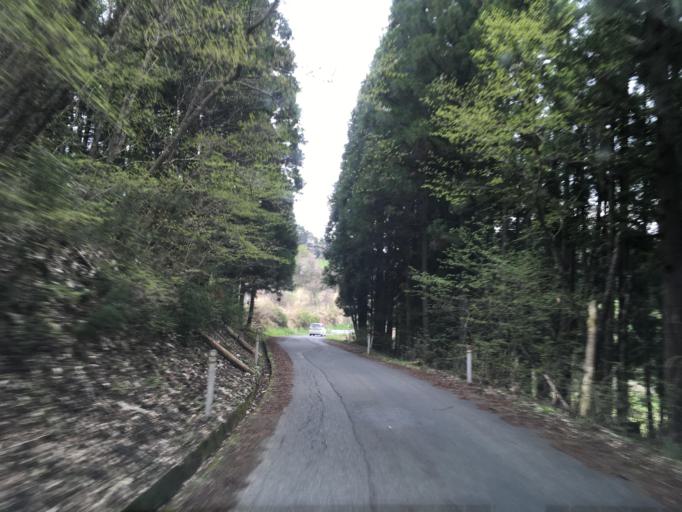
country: JP
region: Iwate
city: Ichinoseki
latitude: 38.8372
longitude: 141.3367
